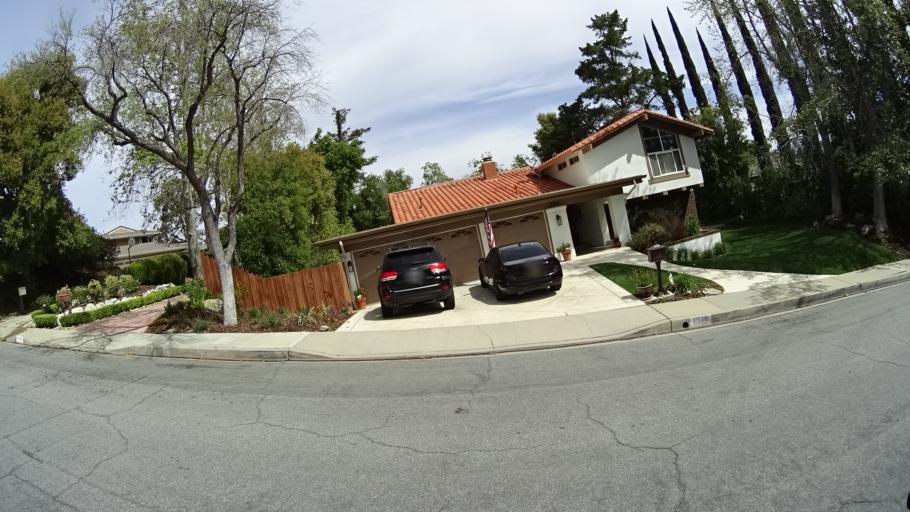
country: US
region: California
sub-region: Ventura County
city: Thousand Oaks
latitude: 34.1537
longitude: -118.8478
